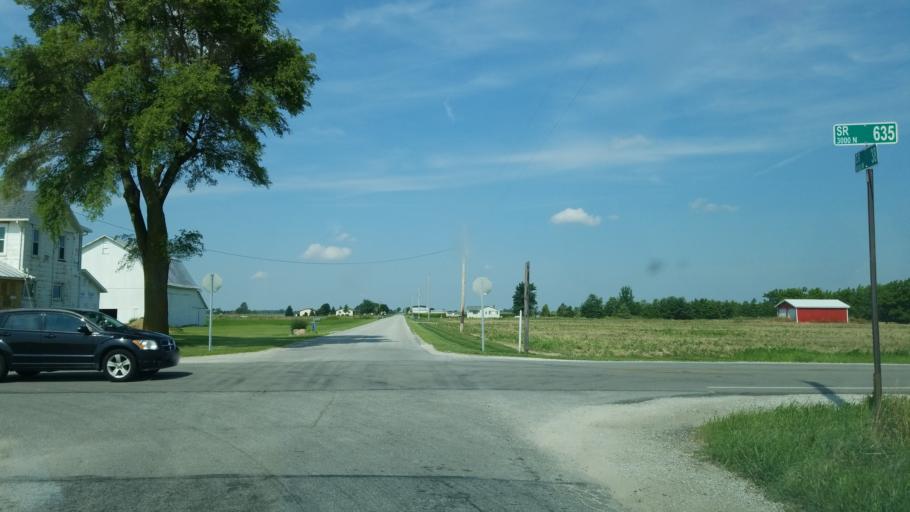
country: US
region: Ohio
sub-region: Seneca County
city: Tiffin
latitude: 41.1667
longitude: -83.2850
